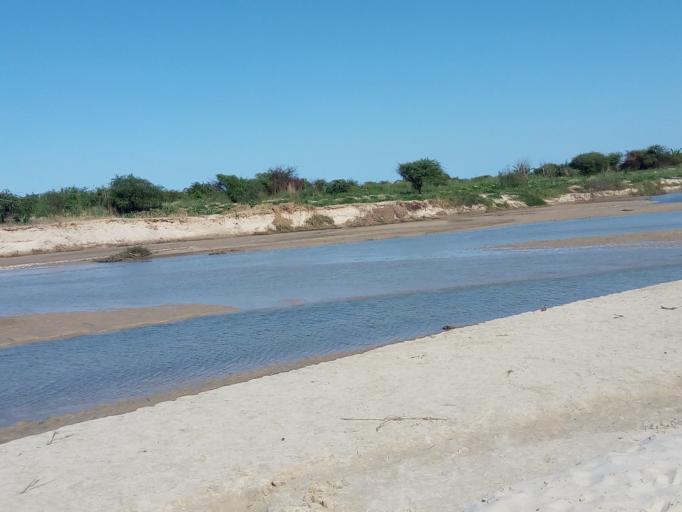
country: MG
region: Menabe
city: Morondava
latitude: -20.3405
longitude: 44.3077
